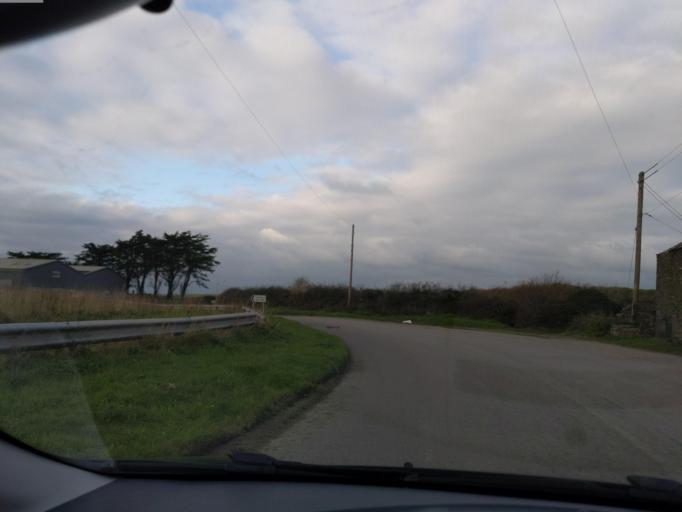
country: GB
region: England
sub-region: Cornwall
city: Padstow
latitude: 50.5360
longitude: -4.9518
